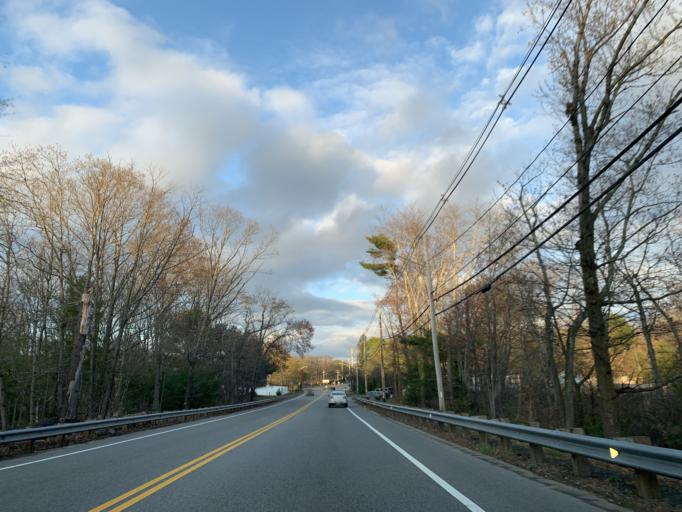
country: US
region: Massachusetts
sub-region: Bristol County
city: Attleboro
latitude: 41.9332
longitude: -71.3256
